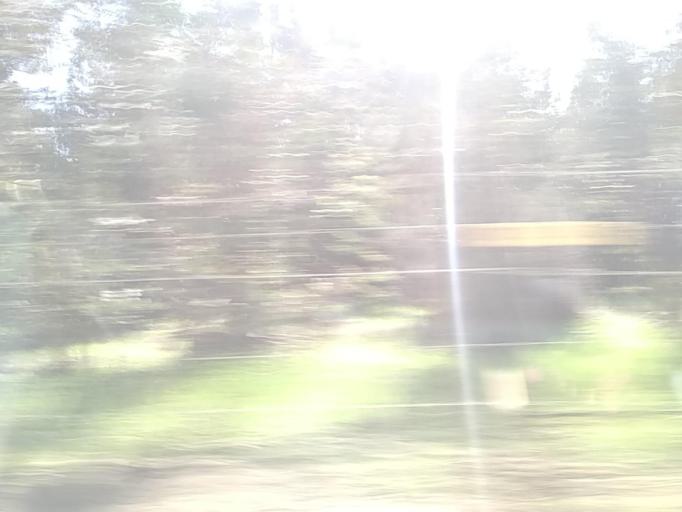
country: CL
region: Valparaiso
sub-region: San Antonio Province
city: El Tabo
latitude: -33.4238
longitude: -71.6303
